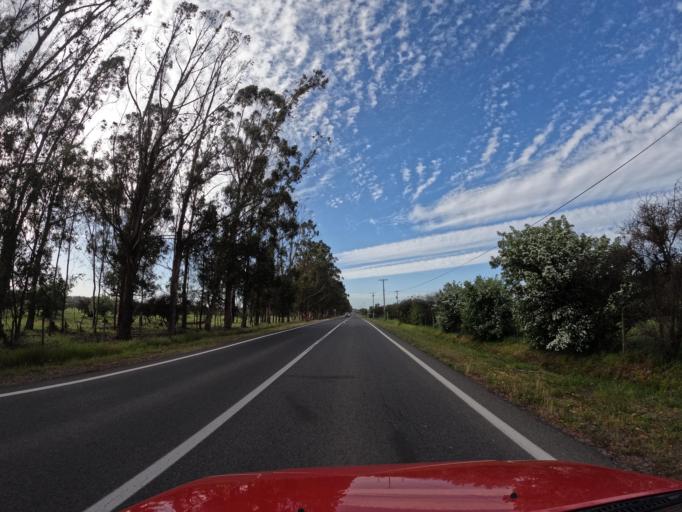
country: CL
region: Valparaiso
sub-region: San Antonio Province
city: San Antonio
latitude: -34.1695
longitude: -71.7312
